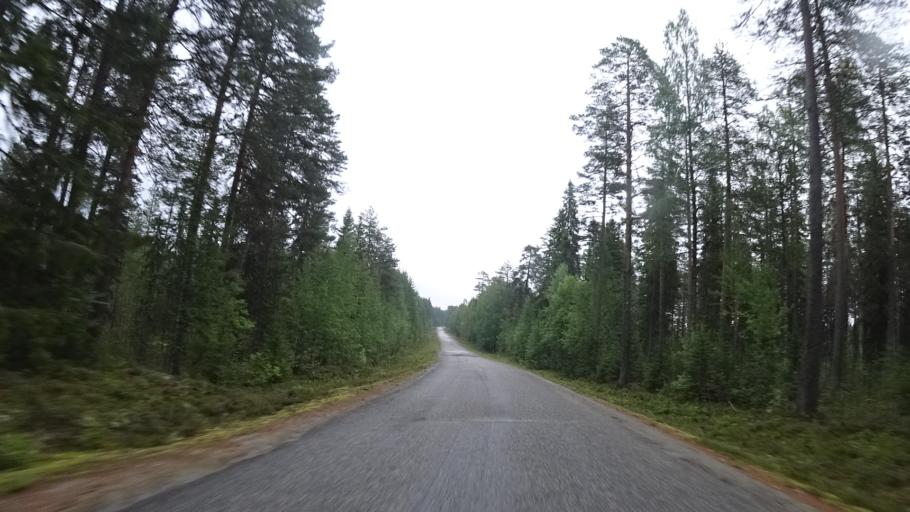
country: FI
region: North Karelia
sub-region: Joensuu
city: Ilomantsi
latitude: 63.2274
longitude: 30.8617
